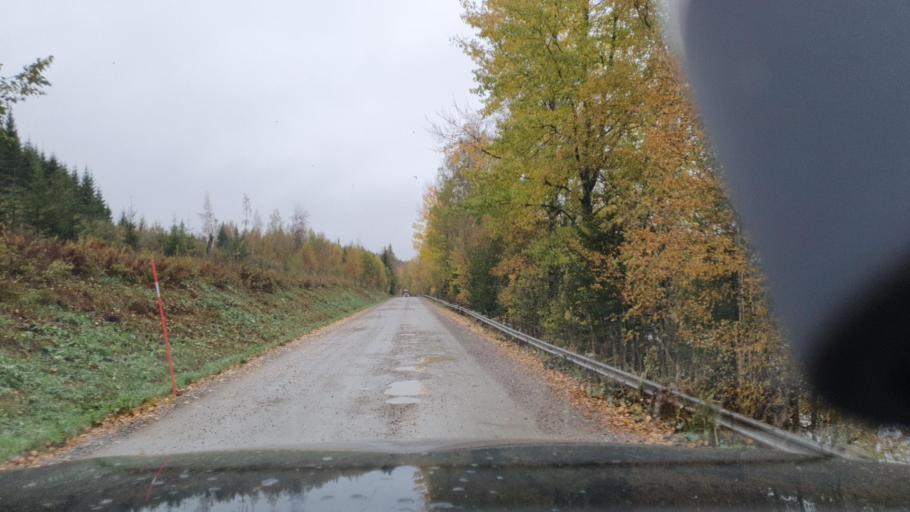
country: SE
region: Vaermland
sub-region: Arvika Kommun
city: Arvika
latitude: 59.8088
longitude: 12.7473
